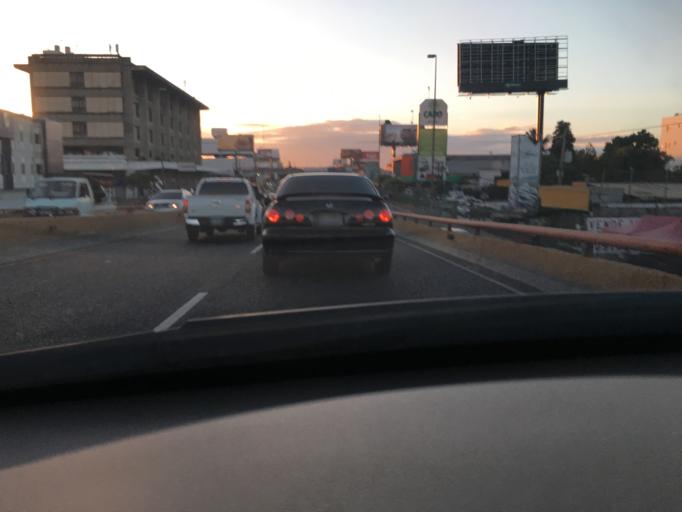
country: DO
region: Nacional
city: La Julia
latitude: 18.4824
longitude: -69.9222
